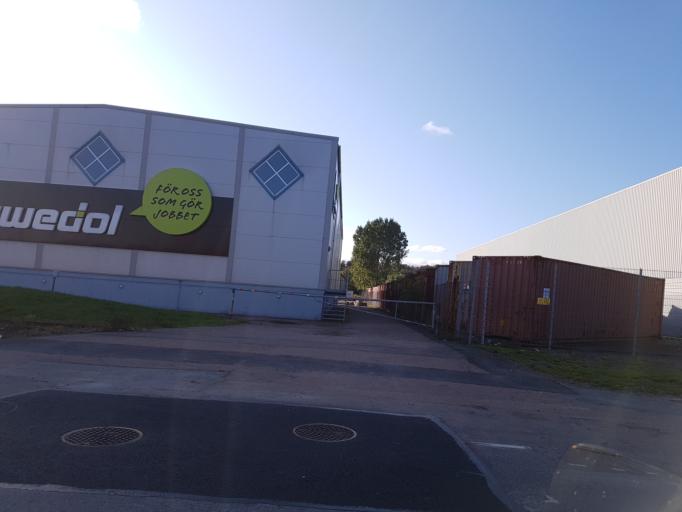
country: SE
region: Vaestra Goetaland
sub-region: Goteborg
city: Goeteborg
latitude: 57.7423
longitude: 11.9942
